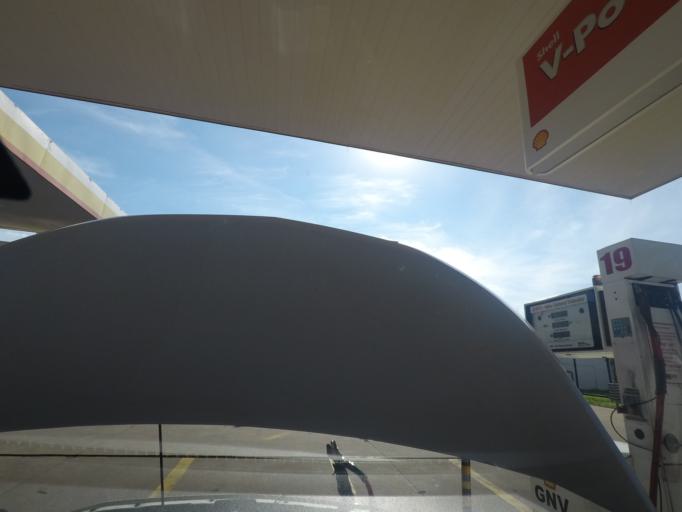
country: BR
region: Sao Paulo
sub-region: Rio Claro
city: Rio Claro
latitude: -22.4166
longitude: -47.5734
